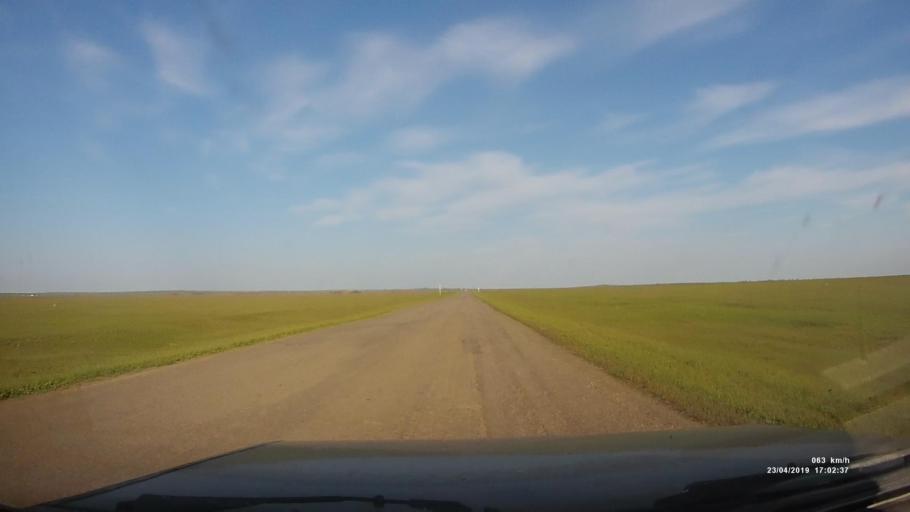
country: RU
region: Kalmykiya
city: Priyutnoye
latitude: 46.2920
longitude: 43.4202
